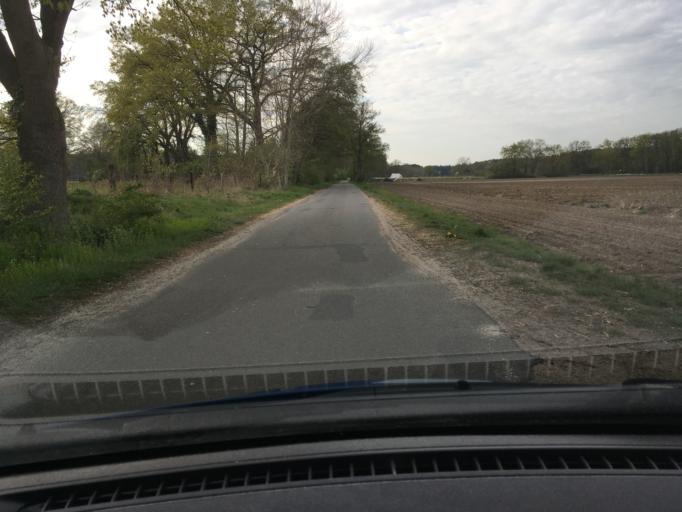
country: DE
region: Lower Saxony
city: Neetze
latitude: 53.2692
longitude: 10.6152
